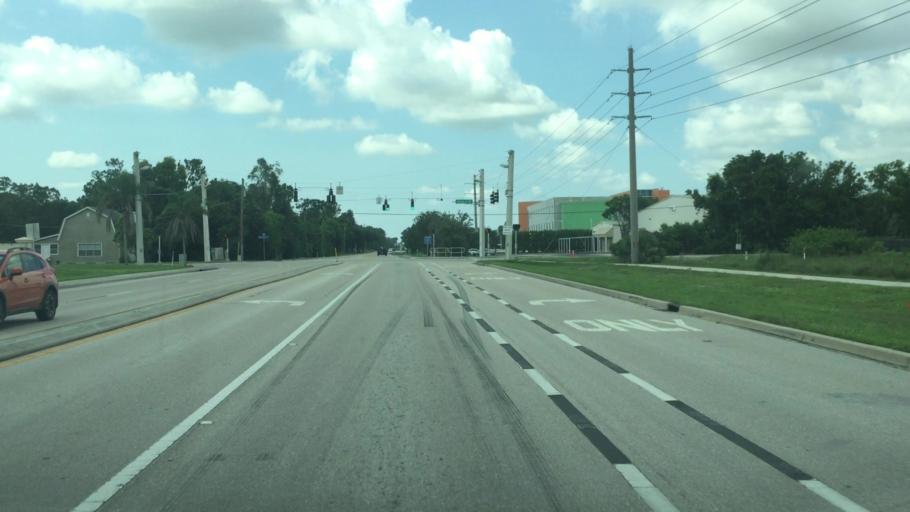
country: US
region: Florida
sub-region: Lee County
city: Pine Manor
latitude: 26.5837
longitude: -81.8474
